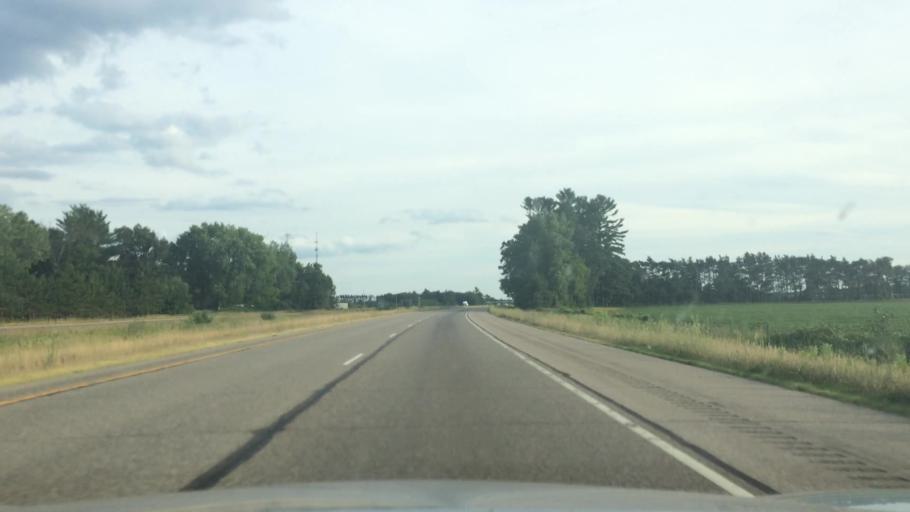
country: US
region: Wisconsin
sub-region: Portage County
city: Plover
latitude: 44.1947
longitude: -89.5234
